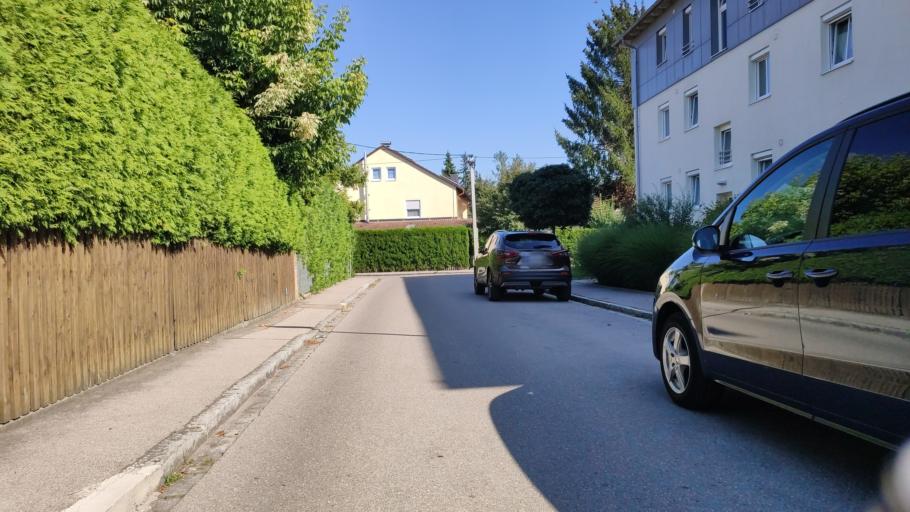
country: DE
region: Bavaria
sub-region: Swabia
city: Konigsbrunn
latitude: 48.2780
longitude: 10.8950
